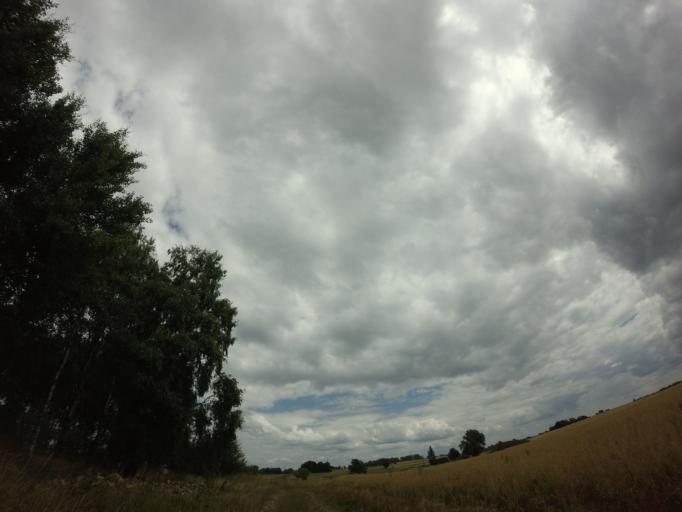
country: PL
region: West Pomeranian Voivodeship
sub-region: Powiat choszczenski
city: Recz
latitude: 53.1818
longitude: 15.5691
